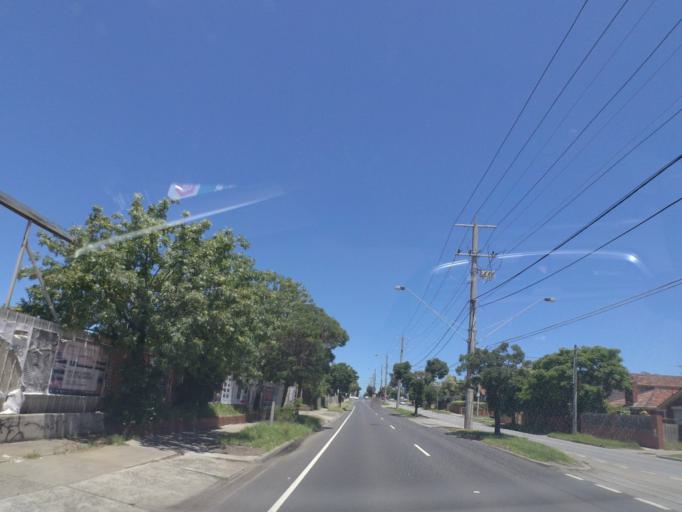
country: AU
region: Victoria
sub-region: Darebin
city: Preston
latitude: -37.7495
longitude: 145.0215
